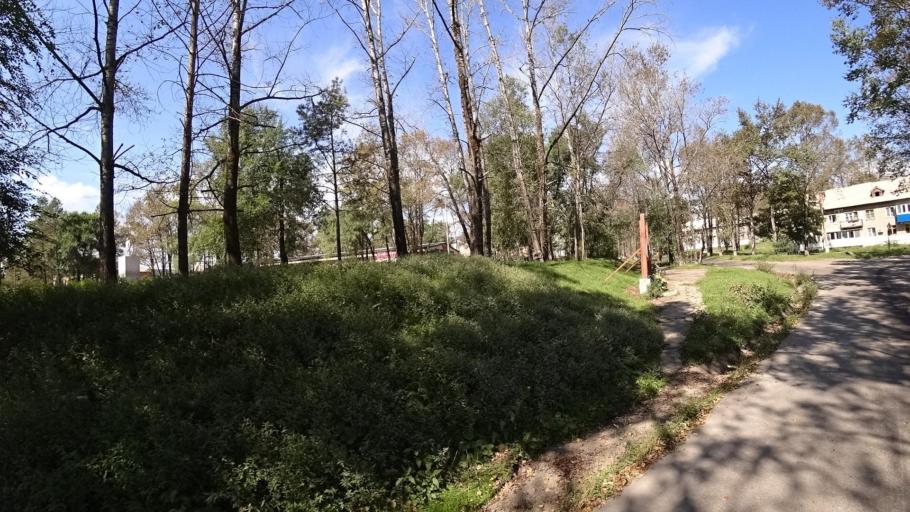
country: RU
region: Jewish Autonomous Oblast
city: Londoko
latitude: 49.0109
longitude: 131.8843
